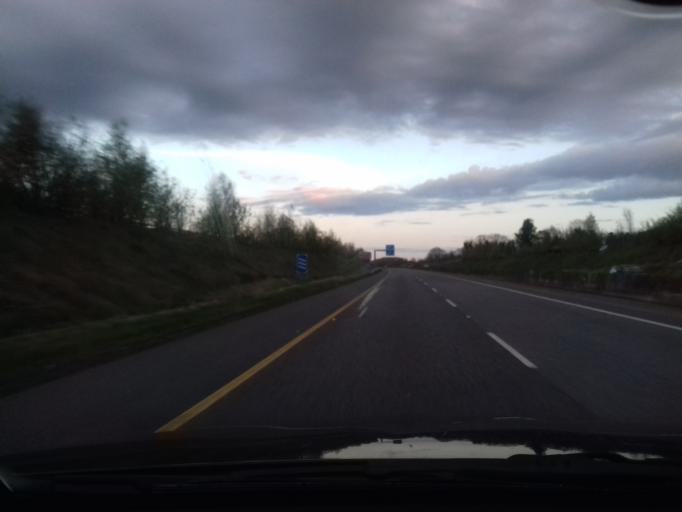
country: IE
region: Leinster
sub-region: An Mhi
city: Navan
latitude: 53.6466
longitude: -6.7481
